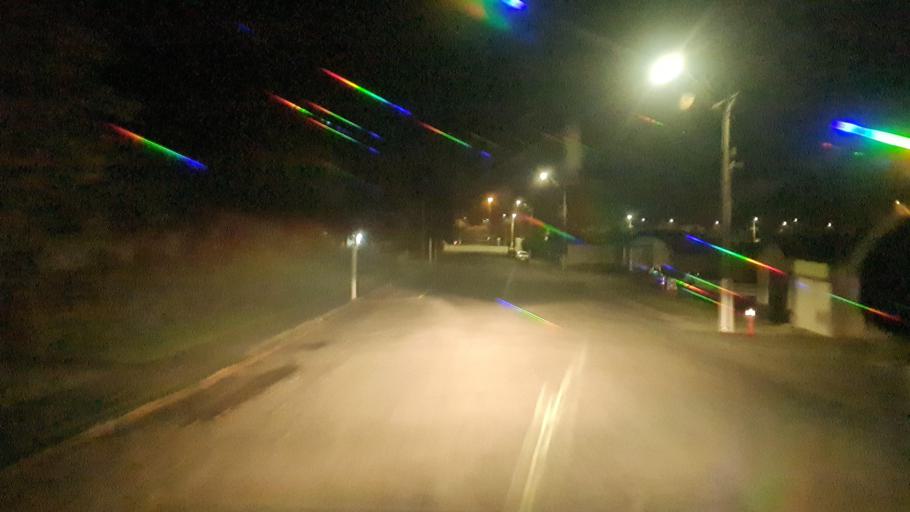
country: NZ
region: Otago
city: Oamaru
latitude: -45.0888
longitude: 170.9727
